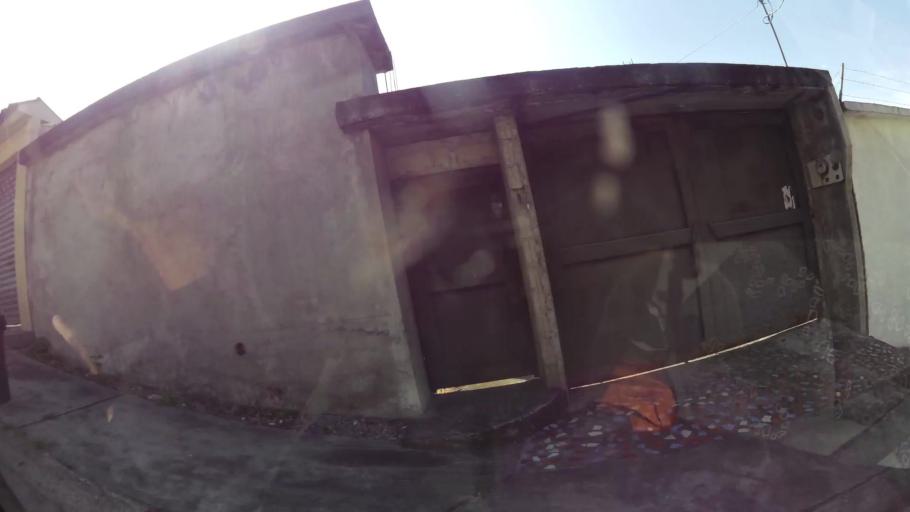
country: EC
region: Guayas
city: Guayaquil
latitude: -2.1854
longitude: -79.9172
